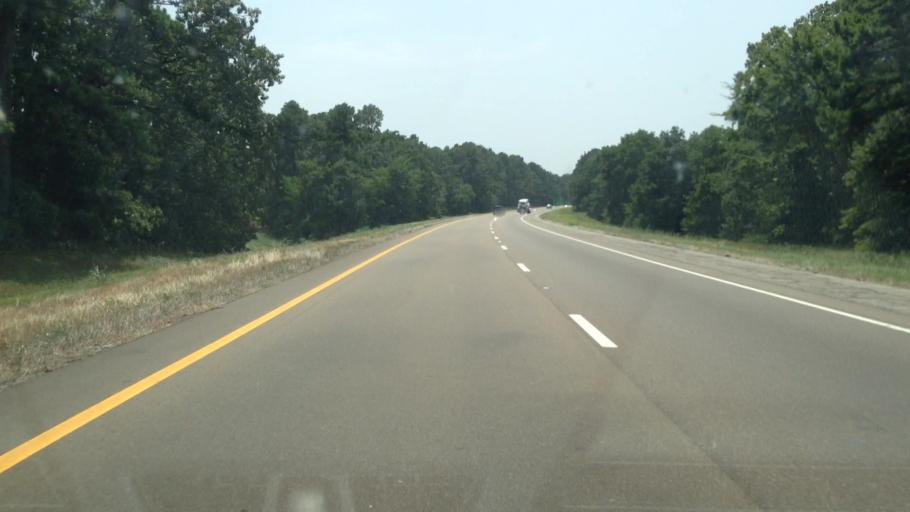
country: US
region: Texas
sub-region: Morris County
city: Naples
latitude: 33.2980
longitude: -94.7157
